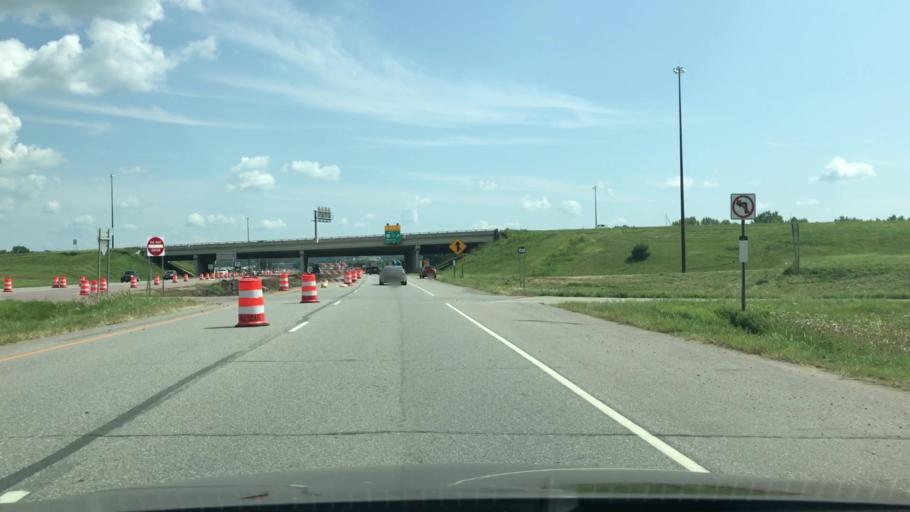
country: US
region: Minnesota
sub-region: Nicollet County
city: North Mankato
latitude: 44.1935
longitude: -94.0185
